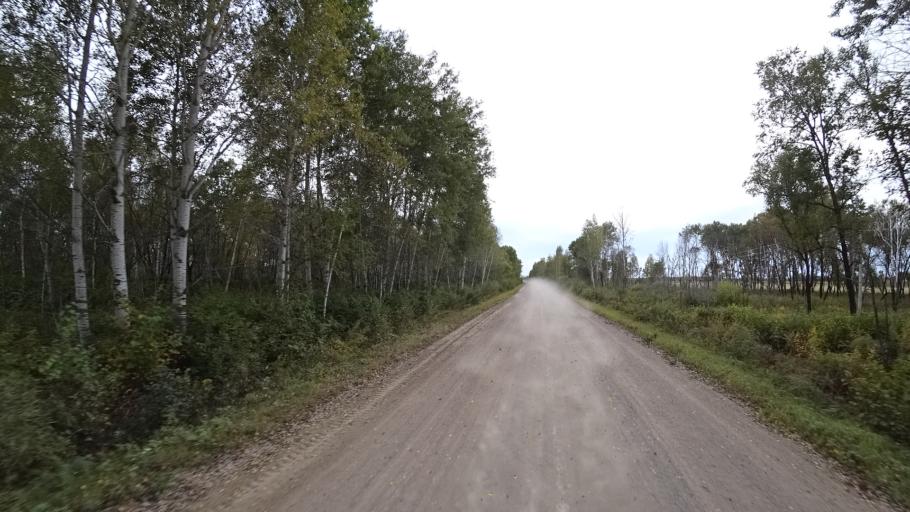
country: RU
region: Amur
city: Arkhara
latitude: 49.3821
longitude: 130.2183
